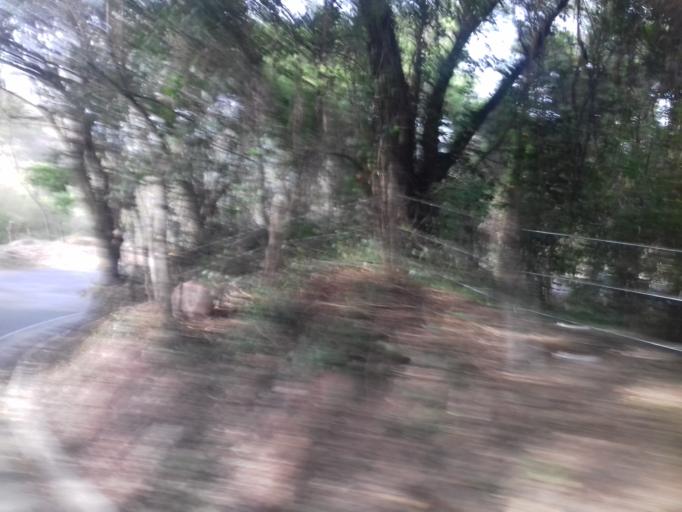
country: CO
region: Antioquia
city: Venecia
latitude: 5.9788
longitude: -75.8259
